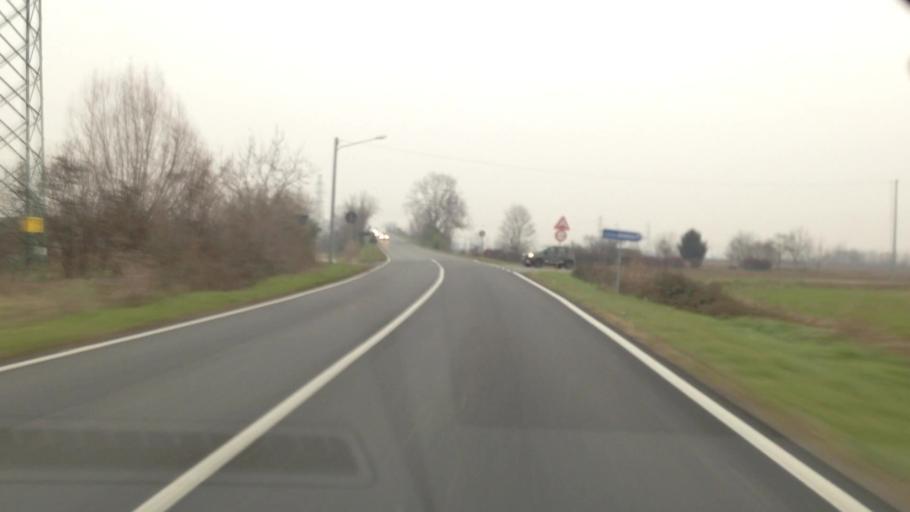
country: IT
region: Piedmont
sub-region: Provincia di Vercelli
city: Livorno Ferraris
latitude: 45.2815
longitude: 8.0652
